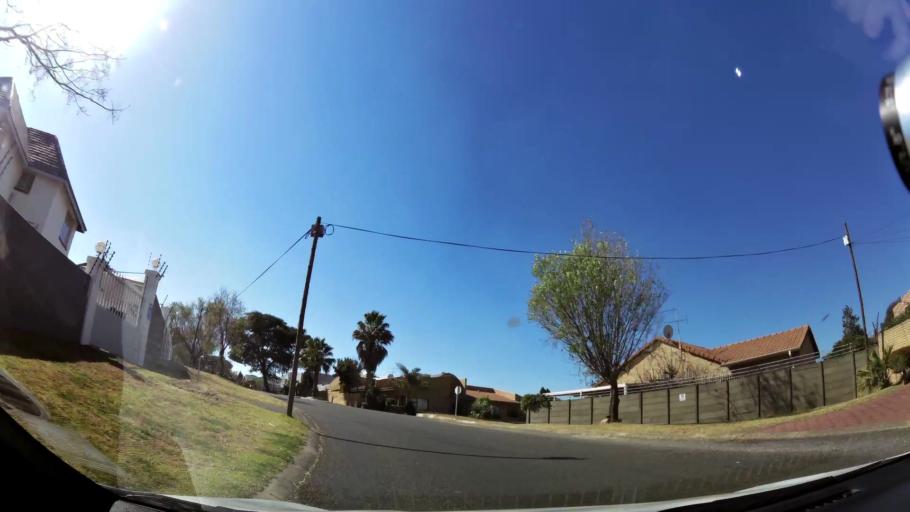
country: ZA
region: Gauteng
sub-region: City of Johannesburg Metropolitan Municipality
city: Johannesburg
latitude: -26.2628
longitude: 27.9972
